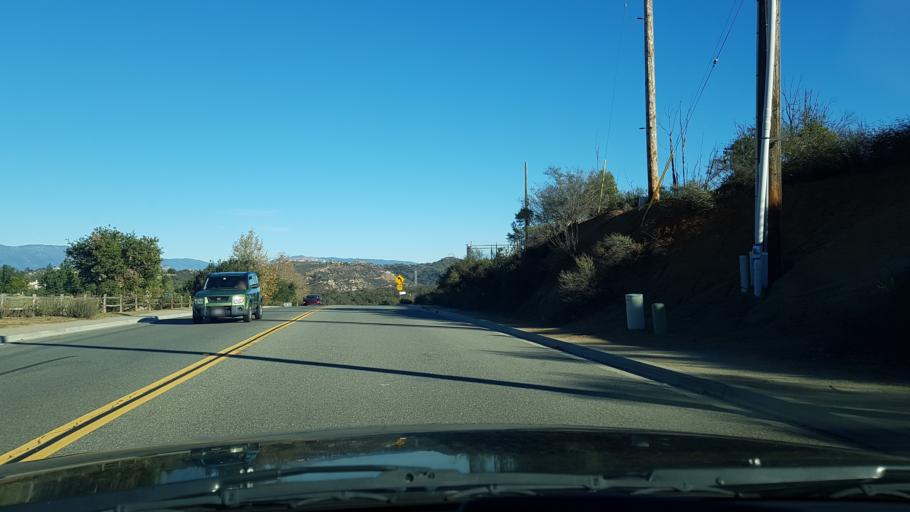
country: US
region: California
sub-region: San Diego County
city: Hidden Meadows
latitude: 33.2119
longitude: -117.1033
